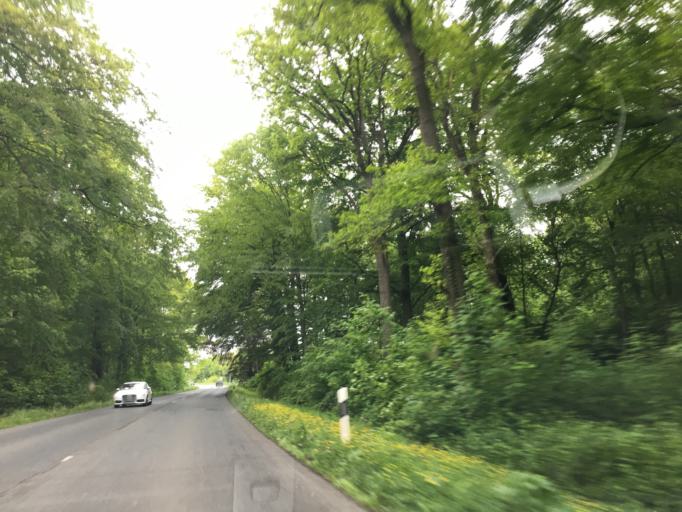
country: DE
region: Lower Saxony
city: Haste
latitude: 52.3792
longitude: 9.4072
